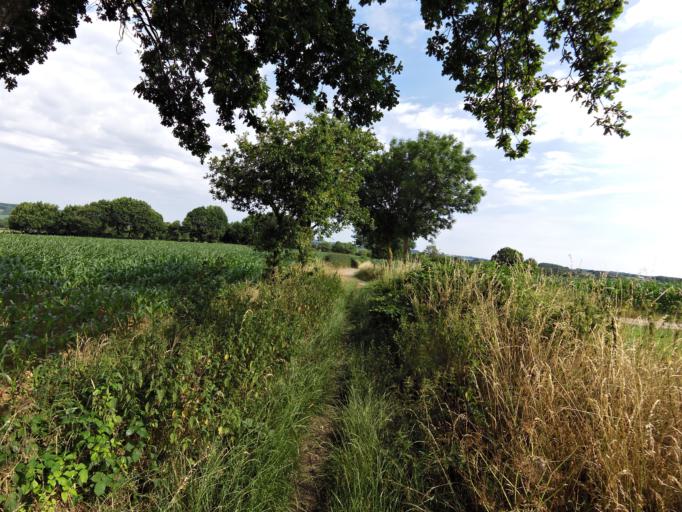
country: BE
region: Wallonia
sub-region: Province de Liege
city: Plombieres
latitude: 50.7850
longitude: 5.9396
